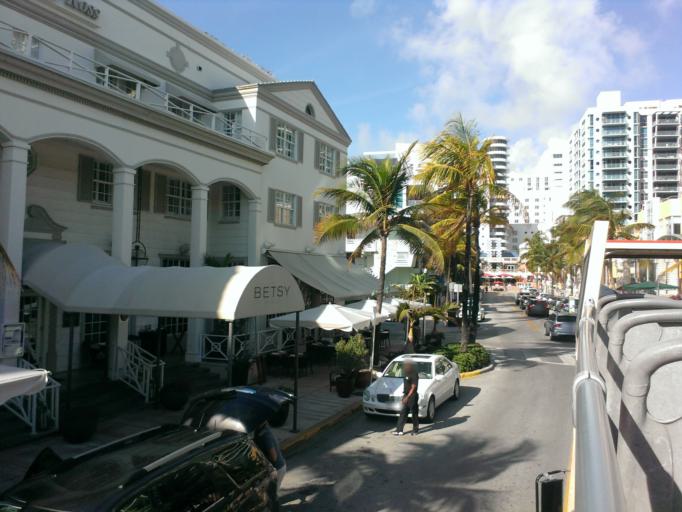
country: US
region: Florida
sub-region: Miami-Dade County
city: Miami Beach
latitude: 25.7864
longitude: -80.1296
